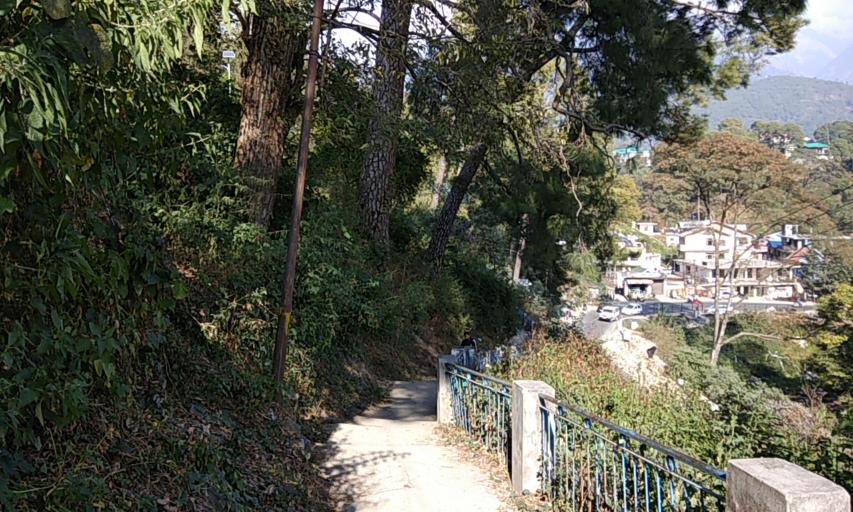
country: IN
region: Himachal Pradesh
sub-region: Kangra
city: Palampur
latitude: 32.1112
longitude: 76.5378
